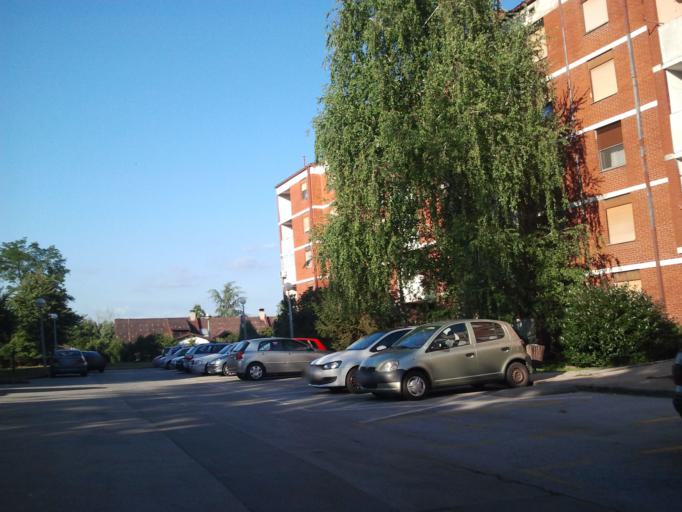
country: HR
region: Sisacko-Moslavacka
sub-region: Grad Sisak
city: Sisak
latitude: 45.4683
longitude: 16.3749
